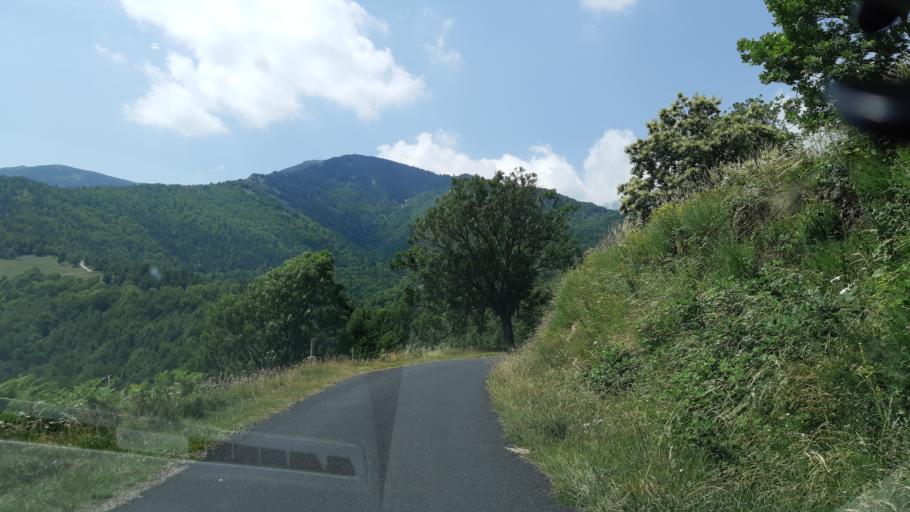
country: FR
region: Languedoc-Roussillon
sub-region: Departement des Pyrenees-Orientales
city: Arles
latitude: 42.5372
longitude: 2.5676
